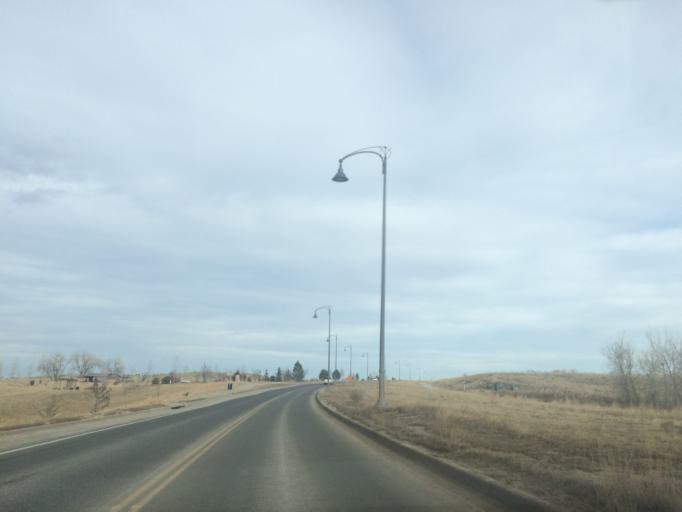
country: US
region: Colorado
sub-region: Boulder County
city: Lafayette
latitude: 39.9798
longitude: -105.0283
